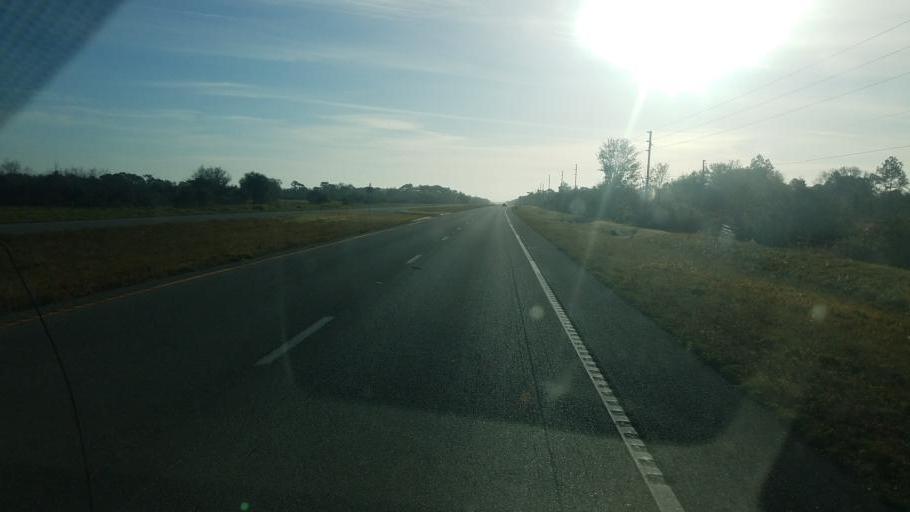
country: US
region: Florida
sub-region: Brevard County
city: June Park
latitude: 28.1268
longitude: -80.9799
